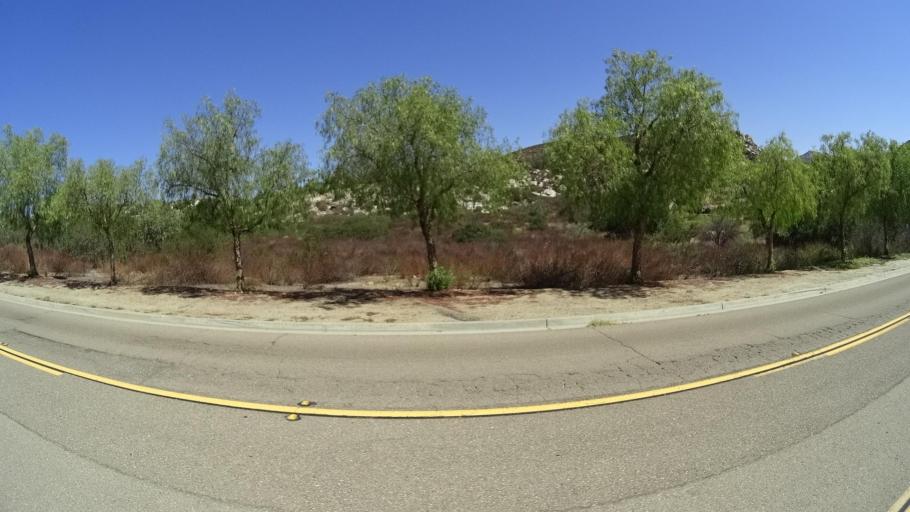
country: US
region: California
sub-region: San Diego County
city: San Diego Country Estates
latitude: 33.0281
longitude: -116.8213
